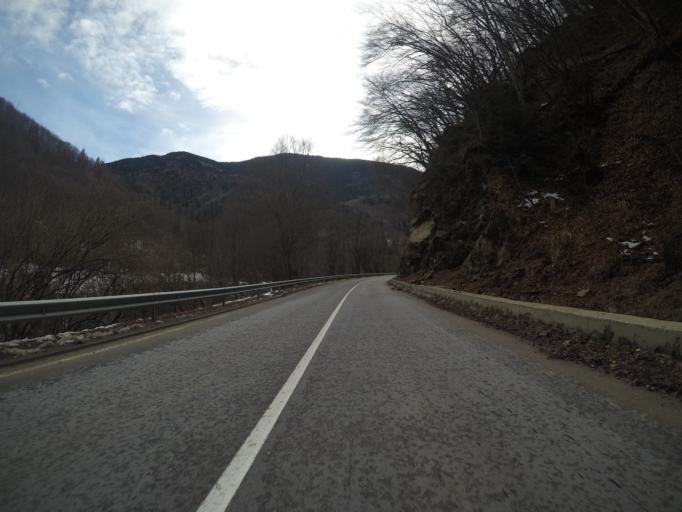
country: BG
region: Kyustendil
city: Sapareva Banya
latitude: 42.1146
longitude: 23.3209
